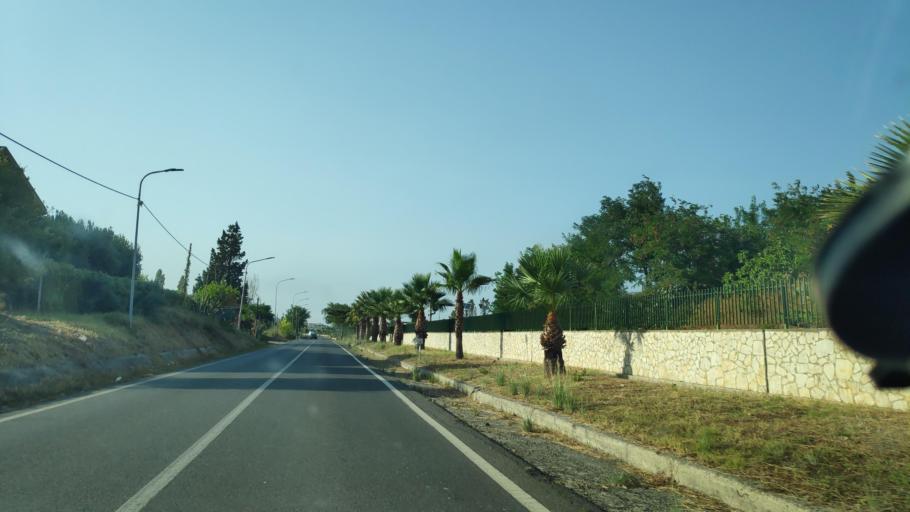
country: IT
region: Calabria
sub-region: Provincia di Catanzaro
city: Santa Caterina dello Ionio Marina
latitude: 38.5236
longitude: 16.5719
